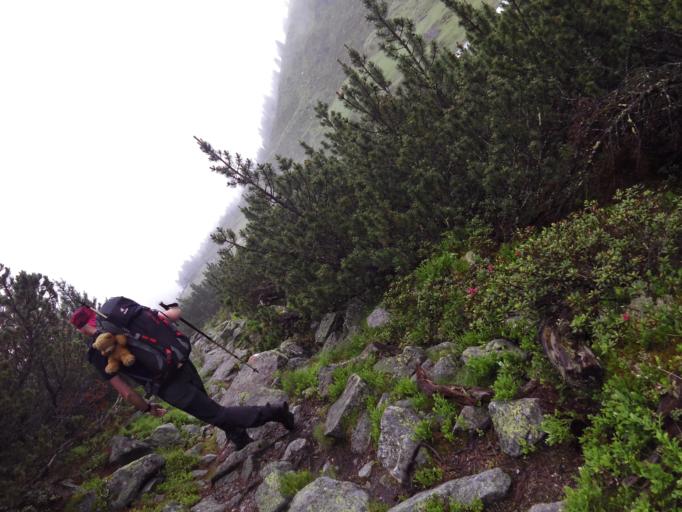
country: AT
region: Tyrol
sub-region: Politischer Bezirk Innsbruck Land
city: Neustift im Stubaital
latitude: 47.0574
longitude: 11.2135
